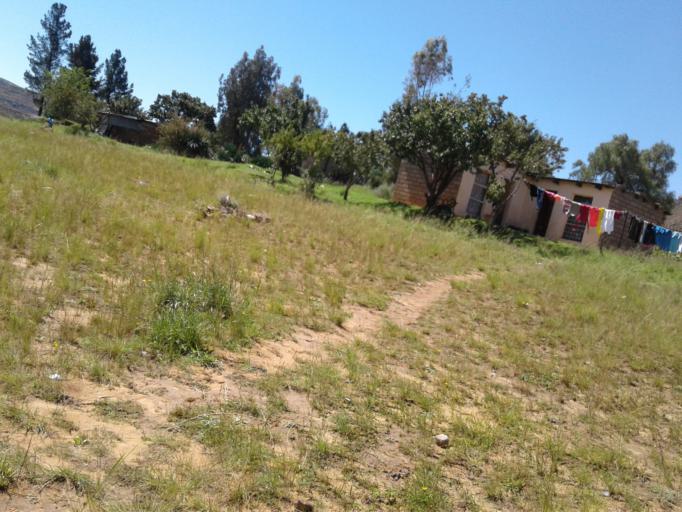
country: LS
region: Quthing
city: Quthing
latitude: -30.3366
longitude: 27.5330
